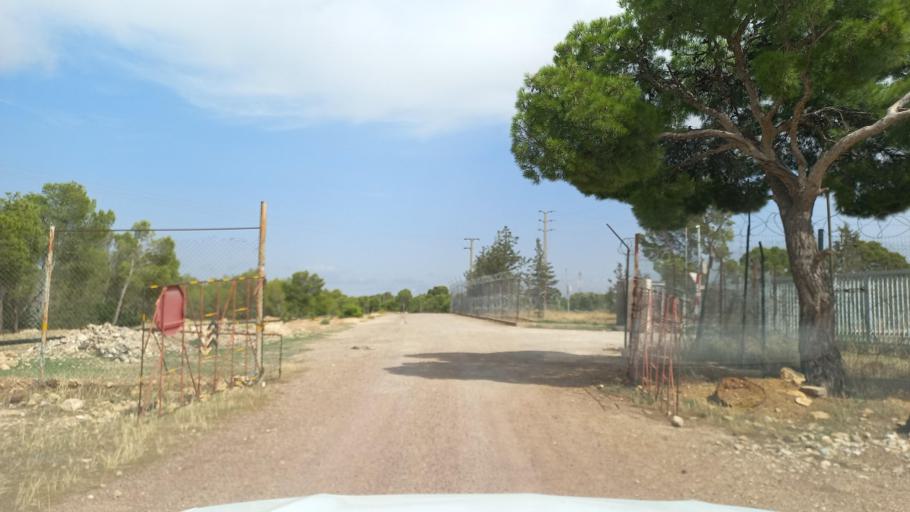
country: TN
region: Al Qasrayn
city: Kasserine
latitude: 35.3832
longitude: 8.8977
